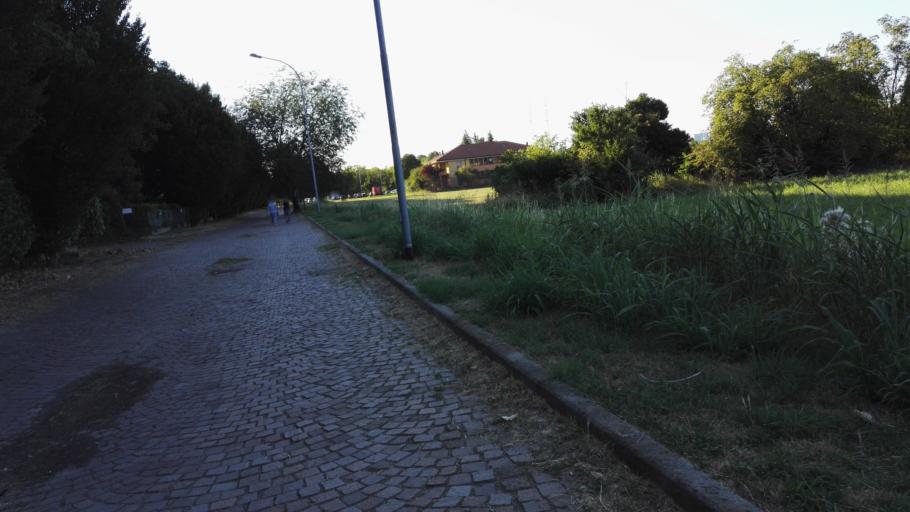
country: IT
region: Lombardy
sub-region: Citta metropolitana di Milano
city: San Giuliano Milanese
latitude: 45.3885
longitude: 9.2964
